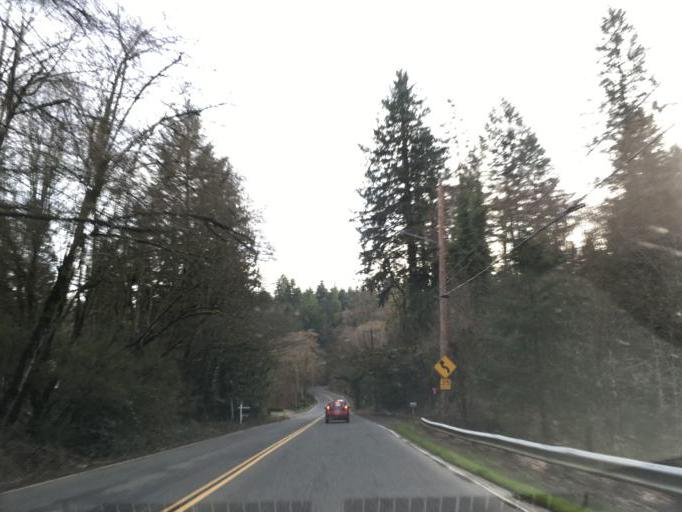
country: US
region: Oregon
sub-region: Clackamas County
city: Lake Oswego
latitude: 45.4486
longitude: -122.6865
